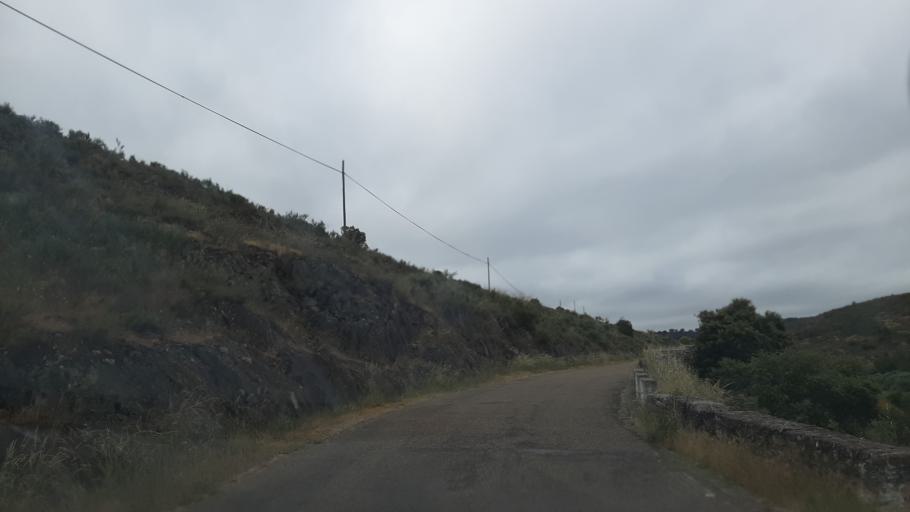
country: ES
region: Castille and Leon
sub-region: Provincia de Salamanca
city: Pastores
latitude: 40.5365
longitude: -6.4841
